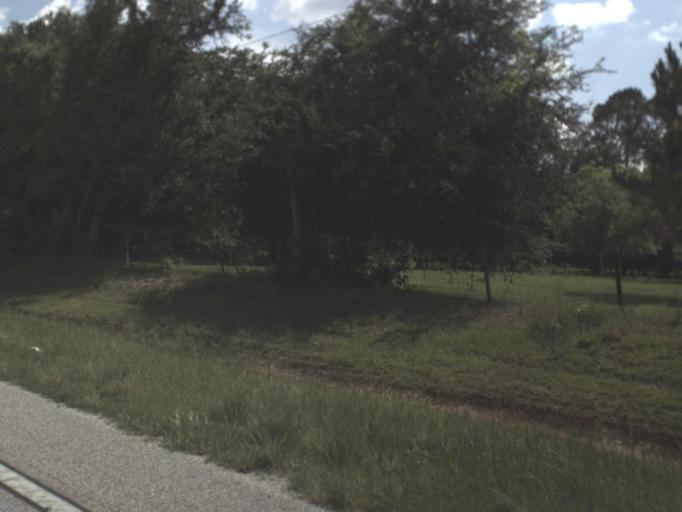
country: US
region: Florida
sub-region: Alachua County
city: Waldo
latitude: 29.8307
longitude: -82.1678
